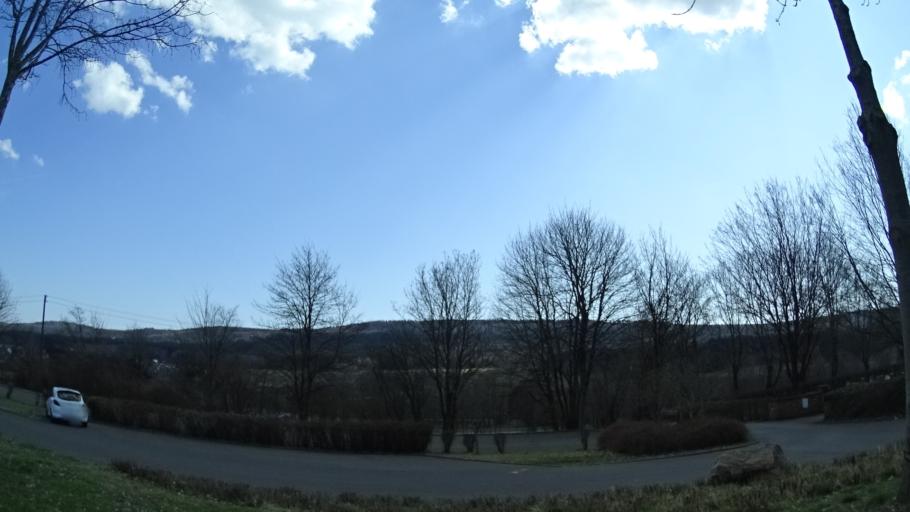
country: DE
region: Rheinland-Pfalz
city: Allenbach
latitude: 49.7531
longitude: 7.1595
